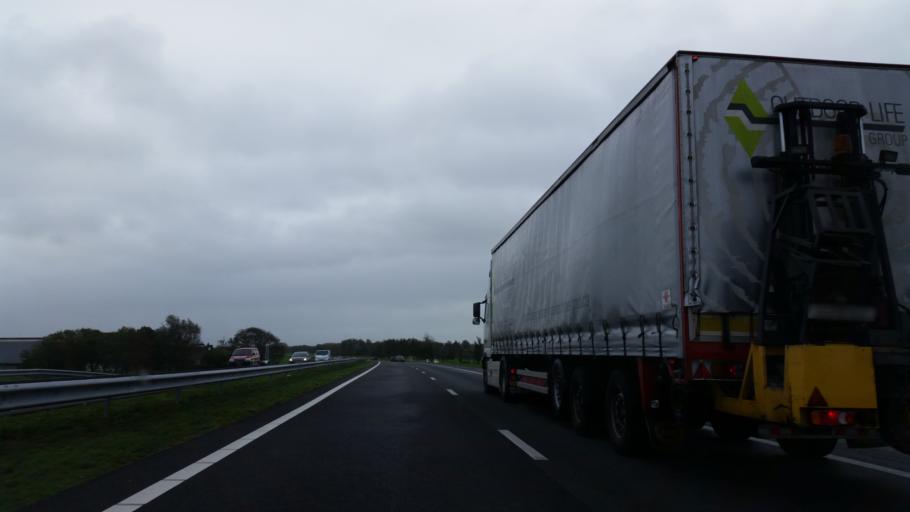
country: NL
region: Friesland
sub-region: Gemeente Skarsterlan
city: Oudehaske
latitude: 53.0050
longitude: 5.8726
